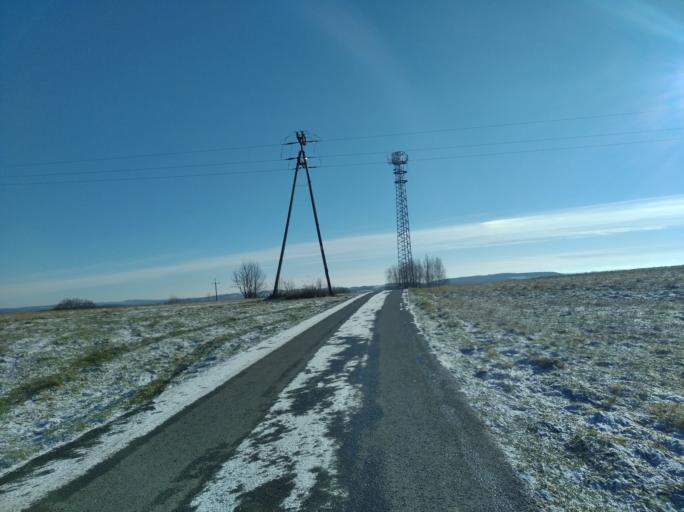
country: PL
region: Subcarpathian Voivodeship
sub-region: Powiat ropczycko-sedziszowski
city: Iwierzyce
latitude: 49.9503
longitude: 21.7616
